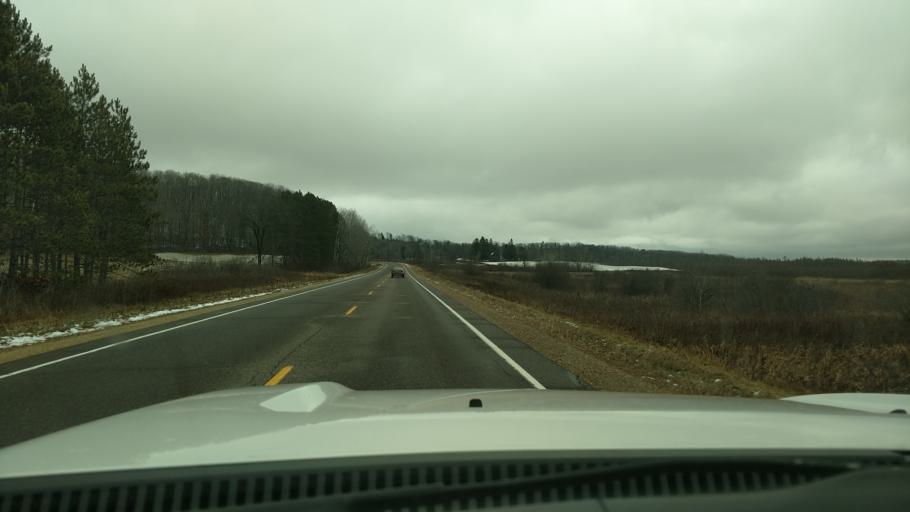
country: US
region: Wisconsin
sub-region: Dunn County
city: Boyceville
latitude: 45.1298
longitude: -92.0074
